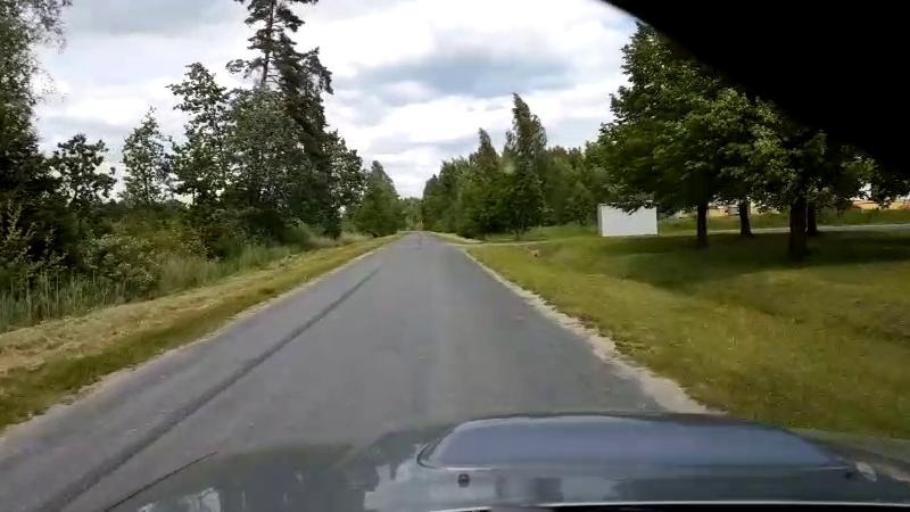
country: EE
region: Paernumaa
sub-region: Halinga vald
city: Parnu-Jaagupi
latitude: 58.5201
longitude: 24.5641
